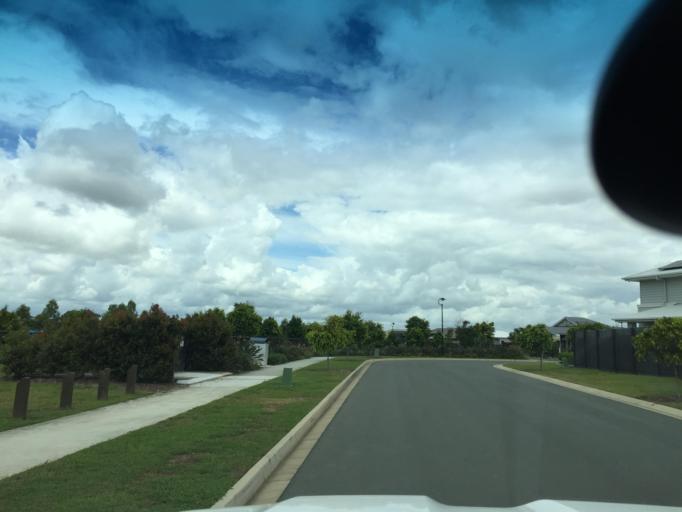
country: AU
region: Queensland
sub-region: Moreton Bay
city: Caboolture South
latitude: -27.0946
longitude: 152.9661
